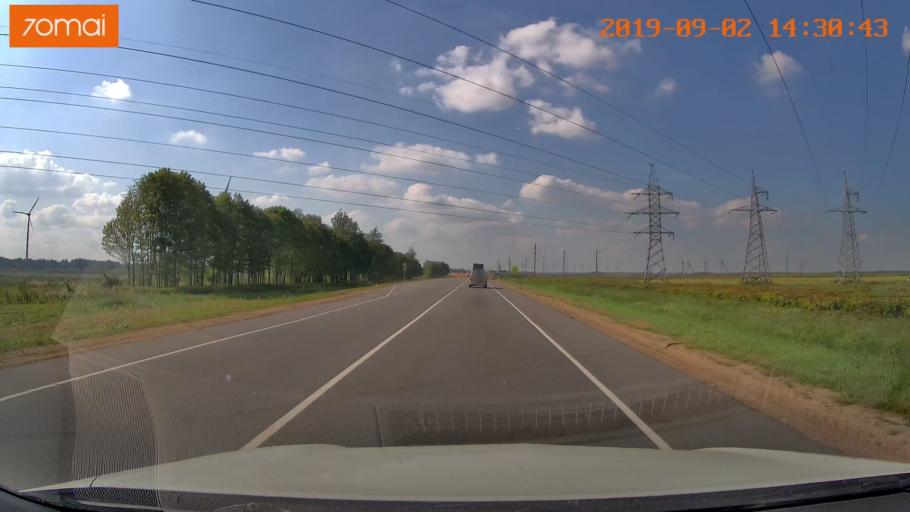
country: BY
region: Mogilev
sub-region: Mahilyowski Rayon
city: Kadino
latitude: 53.8633
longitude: 30.4987
